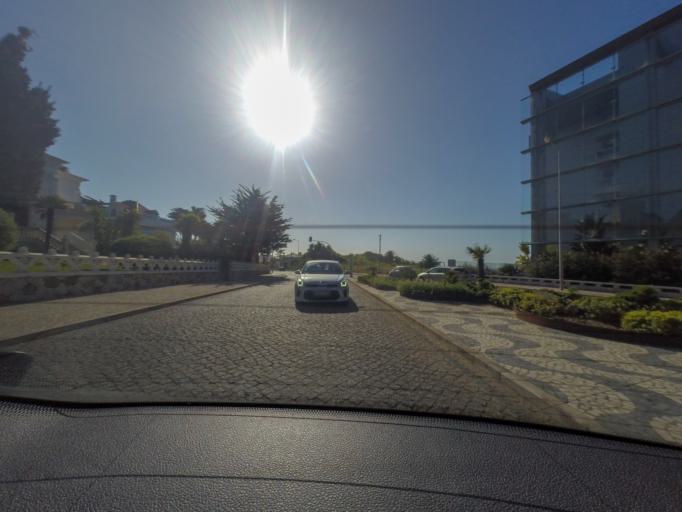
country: PT
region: Lisbon
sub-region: Cascais
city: Estoril
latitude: 38.7043
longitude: -9.4047
